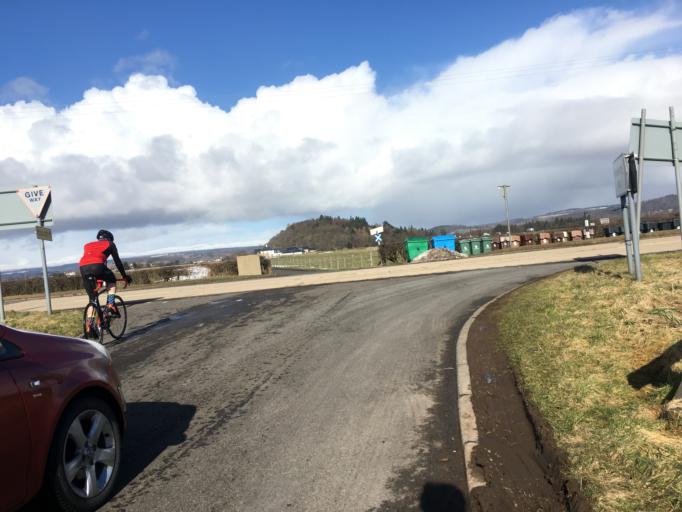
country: GB
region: Scotland
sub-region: Stirling
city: Stirling
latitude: 56.1186
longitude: -3.9739
